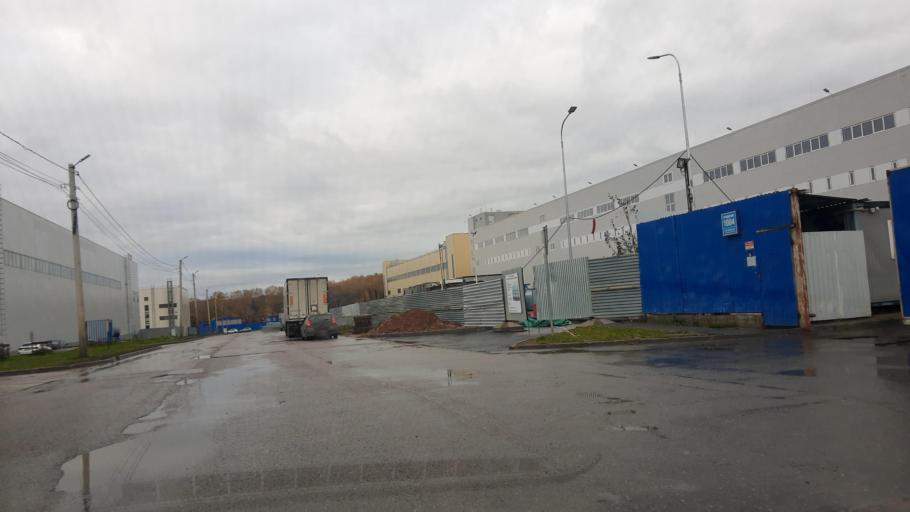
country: RU
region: Moskovskaya
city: Mosrentgen
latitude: 55.6013
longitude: 37.4503
